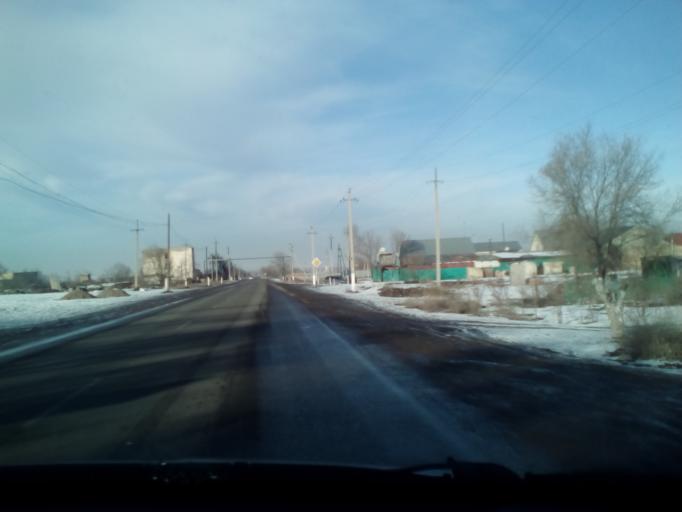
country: KZ
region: Almaty Oblysy
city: Burunday
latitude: 43.1902
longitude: 76.4148
